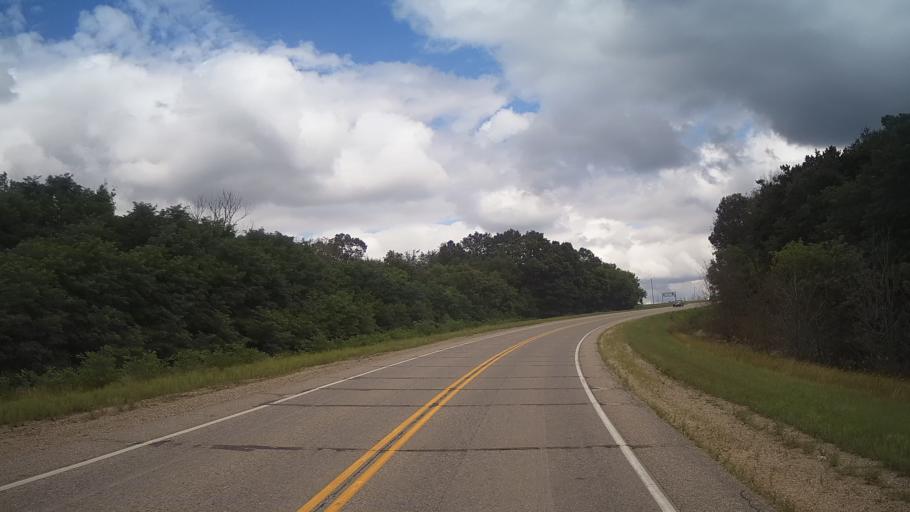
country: US
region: Wisconsin
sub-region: Marquette County
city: Westfield
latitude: 44.0326
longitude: -89.5388
